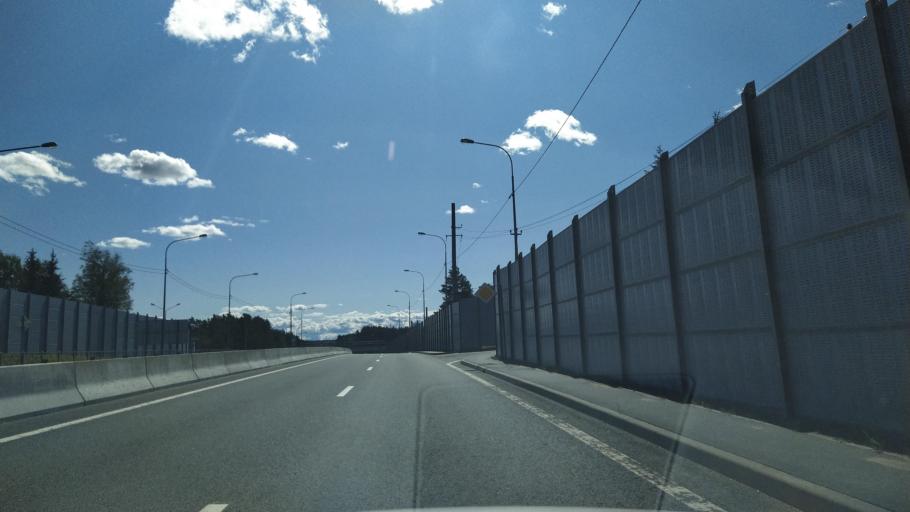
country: RU
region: Leningrad
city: Sapernoye
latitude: 60.6734
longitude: 30.0116
